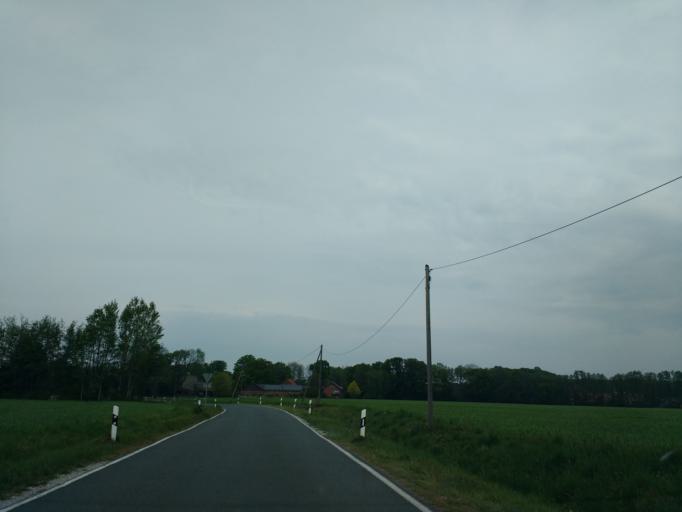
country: DE
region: North Rhine-Westphalia
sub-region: Regierungsbezirk Detmold
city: Delbruck
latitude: 51.8187
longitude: 8.5484
